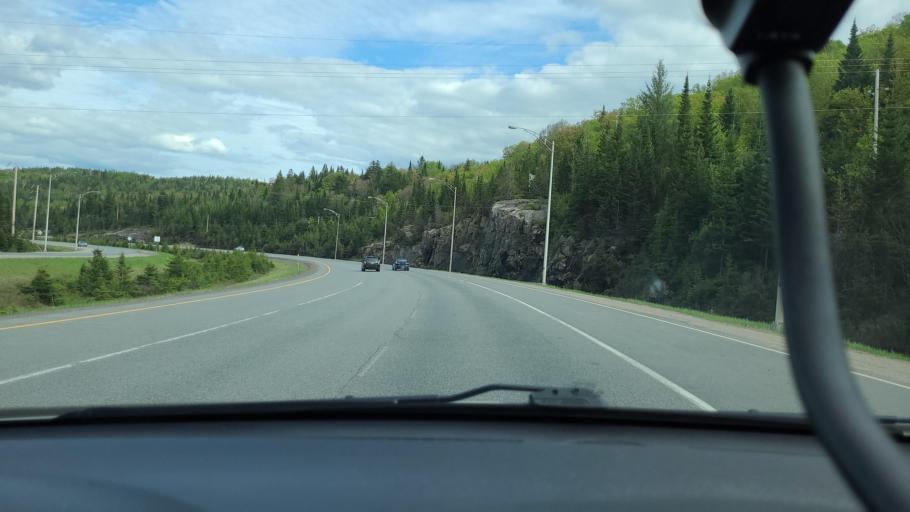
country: CA
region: Quebec
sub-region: Laurentides
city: Sainte-Agathe-des-Monts
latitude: 46.1041
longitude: -74.4148
